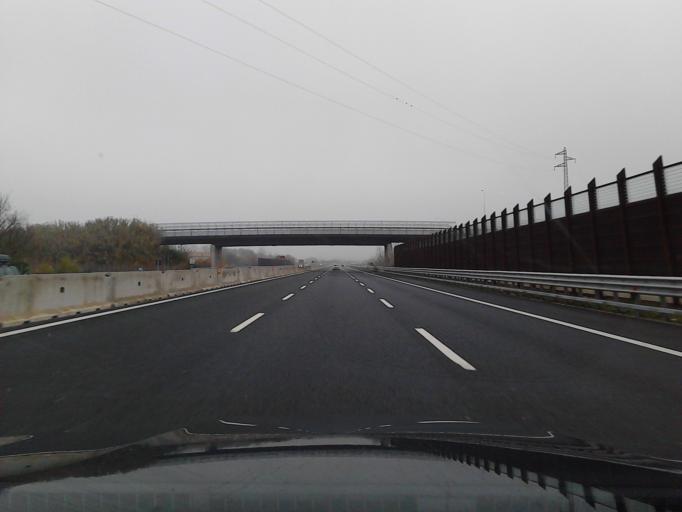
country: IT
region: The Marches
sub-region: Provincia di Pesaro e Urbino
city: Gabicce Mare
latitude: 43.9510
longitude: 12.7604
